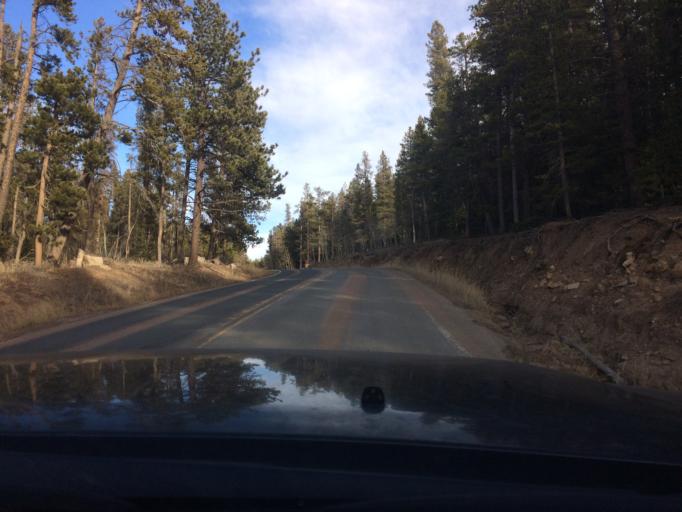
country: US
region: Colorado
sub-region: Boulder County
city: Nederland
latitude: 40.1252
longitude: -105.4376
